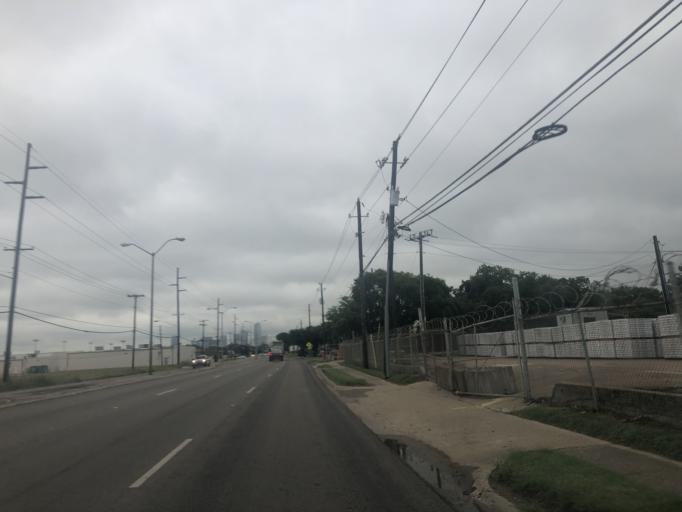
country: US
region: Texas
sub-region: Dallas County
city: Cockrell Hill
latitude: 32.7786
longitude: -96.8623
